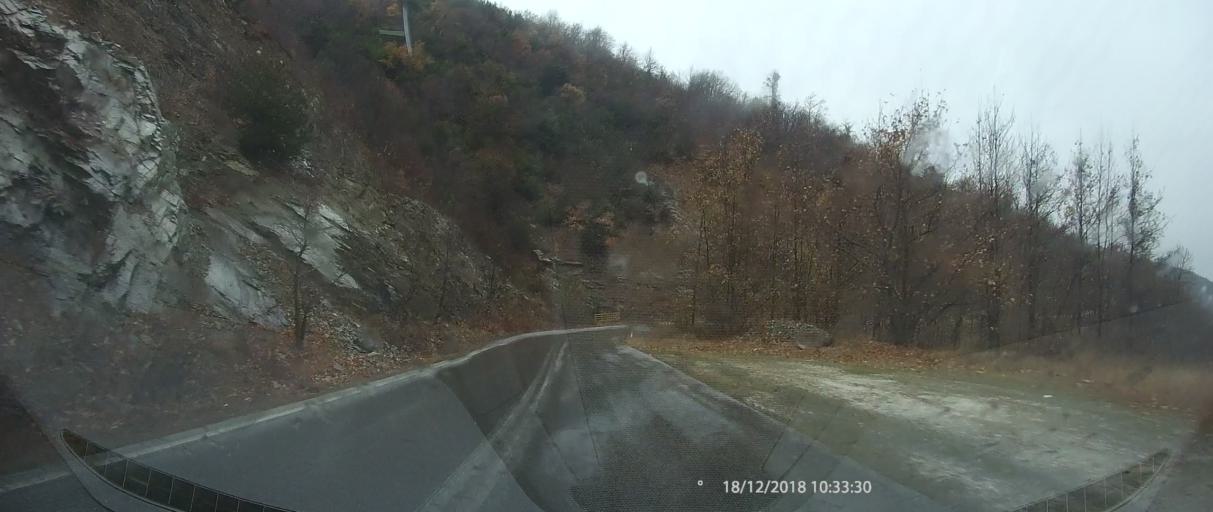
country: GR
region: Central Macedonia
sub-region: Nomos Pierias
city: Kato Milia
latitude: 40.1985
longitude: 22.3006
